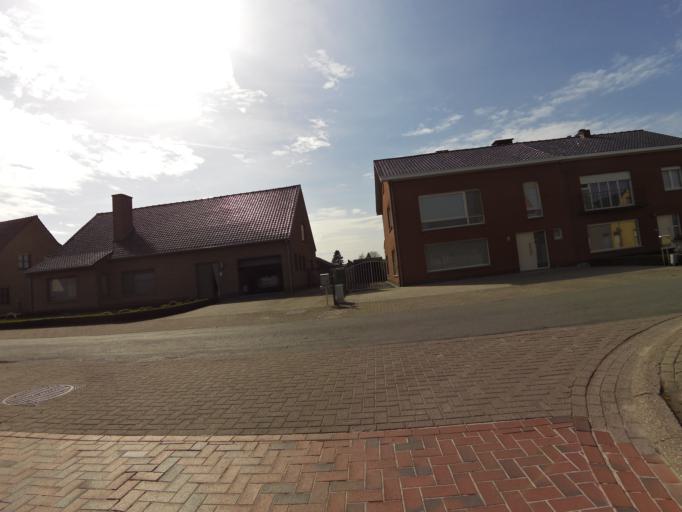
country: BE
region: Flanders
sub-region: Provincie West-Vlaanderen
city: Koekelare
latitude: 51.0867
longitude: 2.9761
